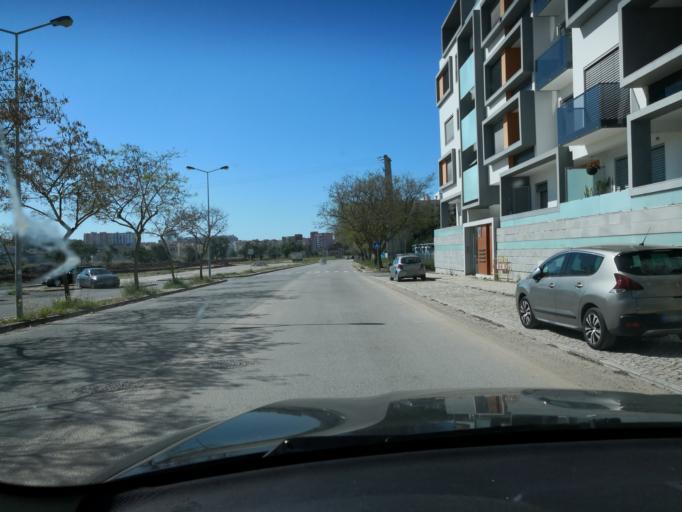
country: PT
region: Setubal
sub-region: Setubal
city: Setubal
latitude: 38.5389
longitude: -8.8897
